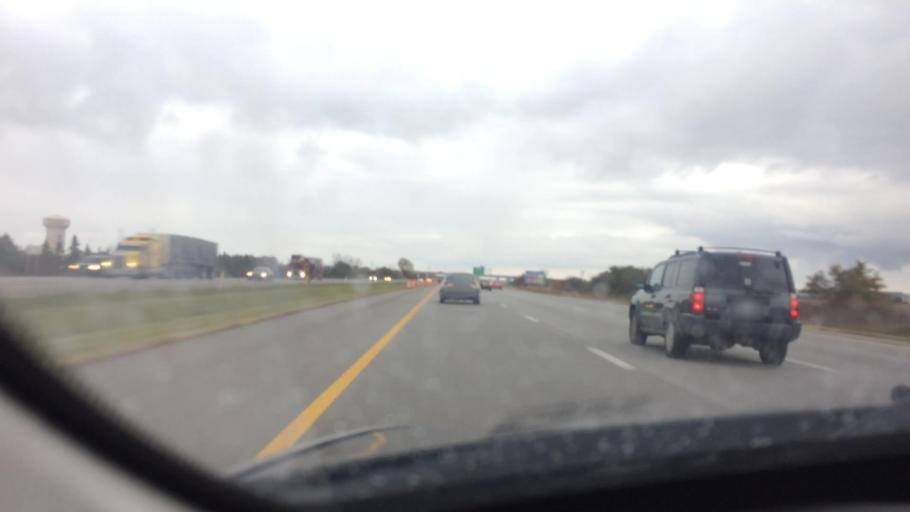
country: US
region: Ohio
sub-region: Wood County
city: Bowling Green
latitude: 41.3578
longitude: -83.6209
